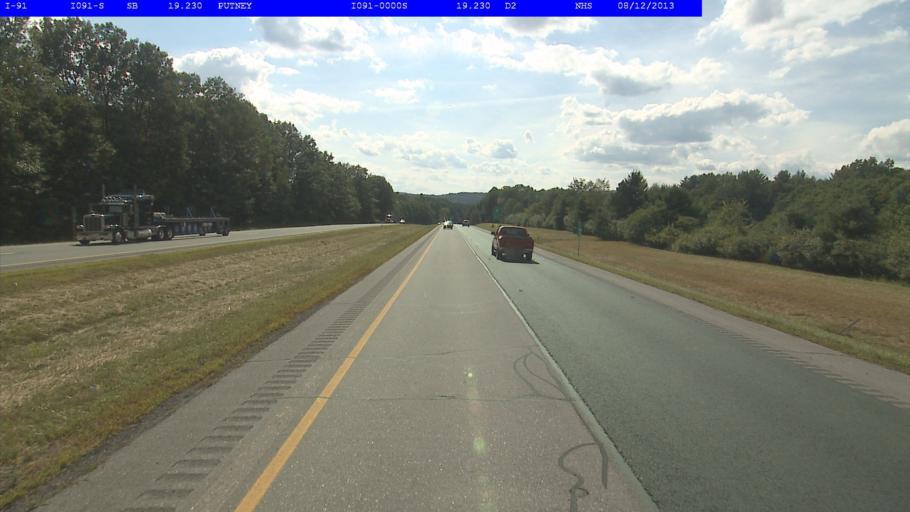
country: US
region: New Hampshire
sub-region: Cheshire County
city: Westmoreland
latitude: 42.9680
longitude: -72.5005
